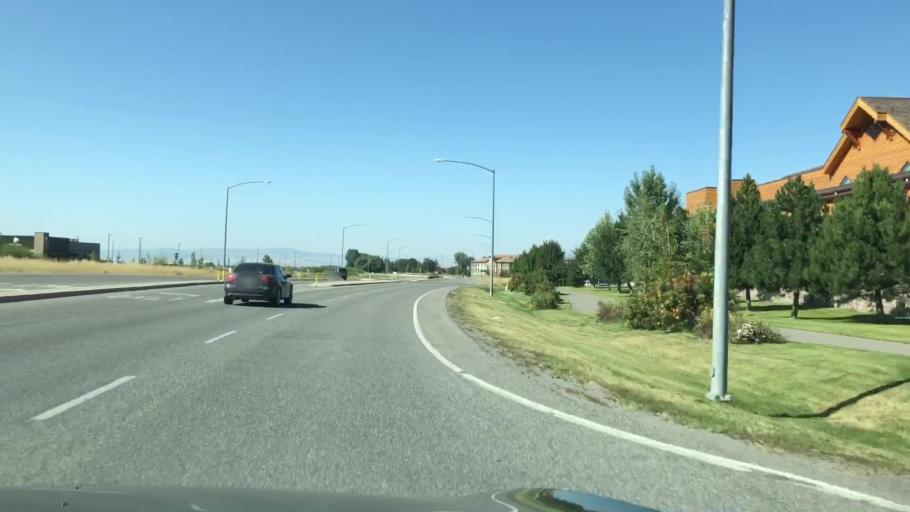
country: US
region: Montana
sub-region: Gallatin County
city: Bozeman
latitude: 45.7138
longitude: -111.0681
